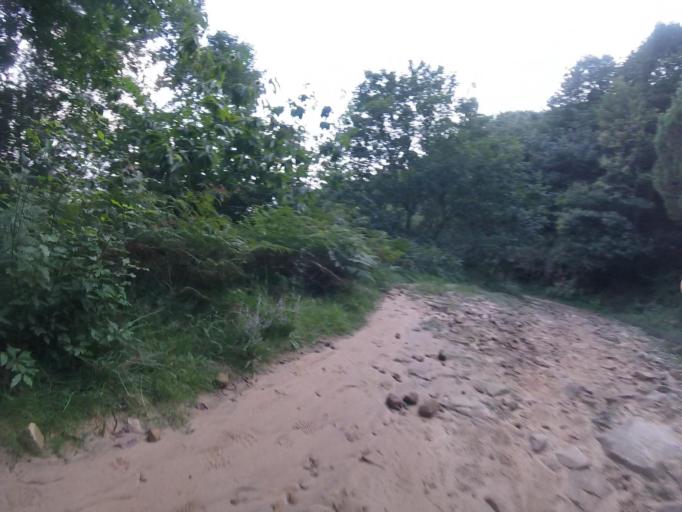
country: ES
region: Basque Country
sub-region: Provincia de Guipuzcoa
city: Lezo
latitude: 43.3418
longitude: -1.8507
